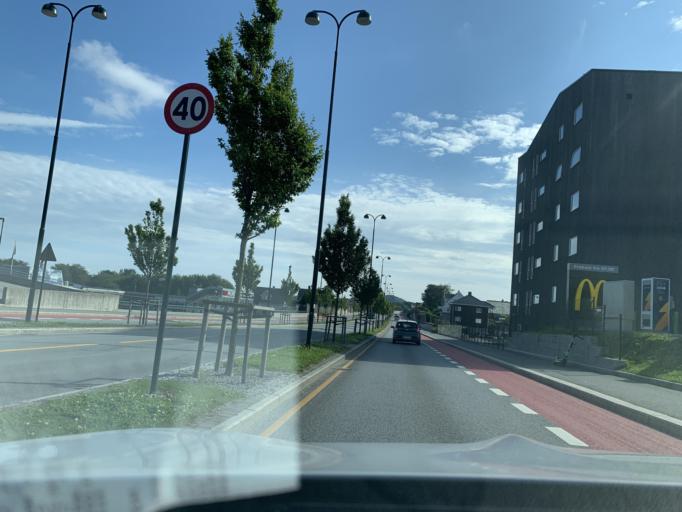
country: NO
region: Rogaland
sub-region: Stavanger
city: Stavanger
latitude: 58.9337
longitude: 5.7400
